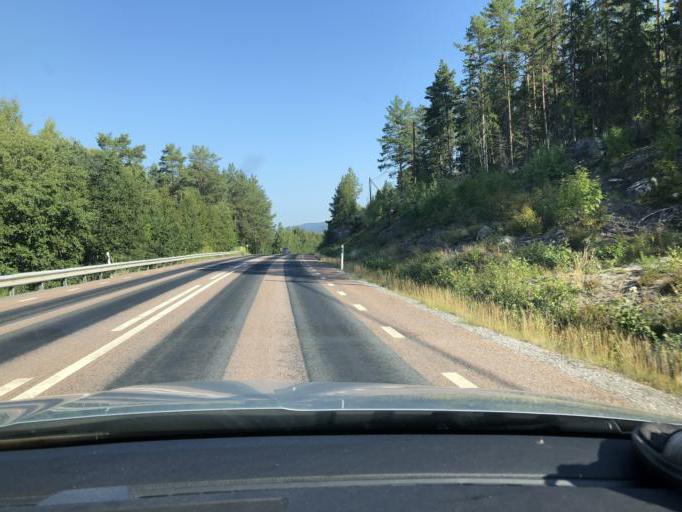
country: SE
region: Vaesternorrland
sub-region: Kramfors Kommun
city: Kramfors
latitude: 62.8914
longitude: 17.9048
